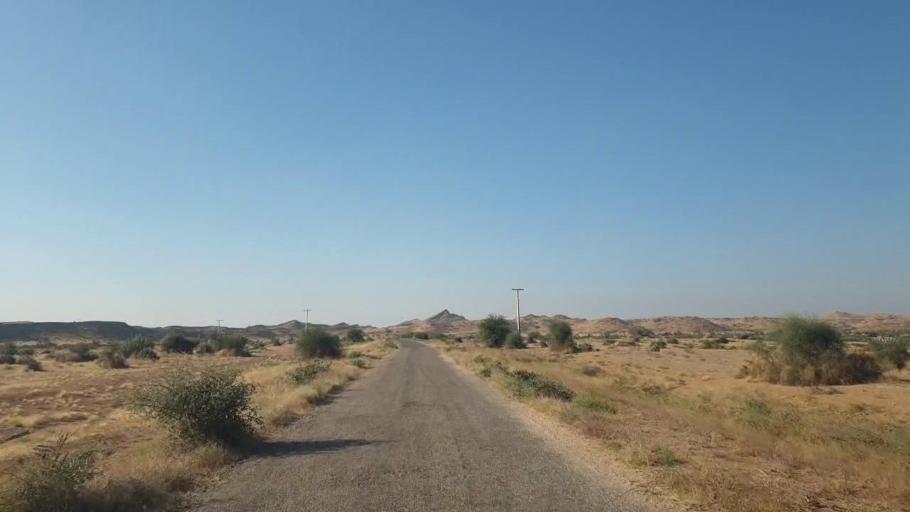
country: PK
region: Sindh
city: Malir Cantonment
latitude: 25.3969
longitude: 67.4944
